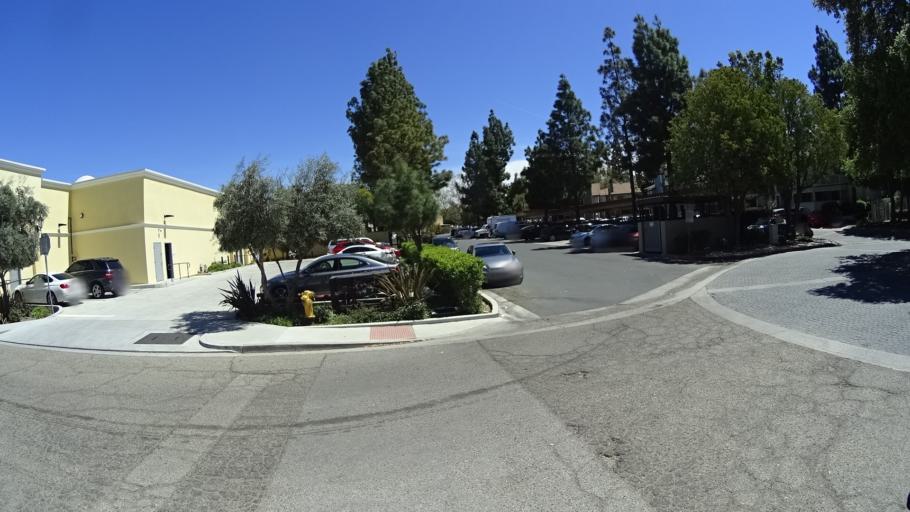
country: US
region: California
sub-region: Ventura County
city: Thousand Oaks
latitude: 34.1737
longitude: -118.8436
